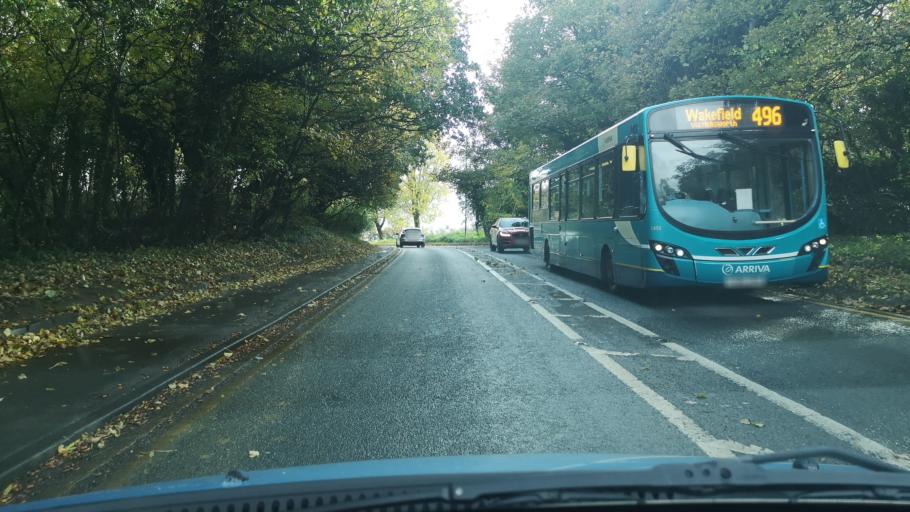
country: GB
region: England
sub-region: City and Borough of Wakefield
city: Hemsworth
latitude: 53.6208
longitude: -1.3630
